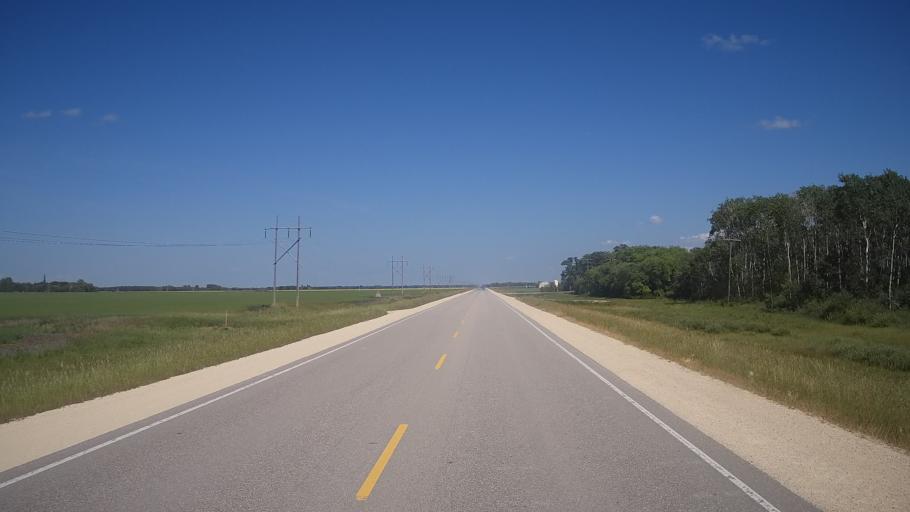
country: CA
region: Manitoba
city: Stonewall
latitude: 50.1227
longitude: -97.4264
